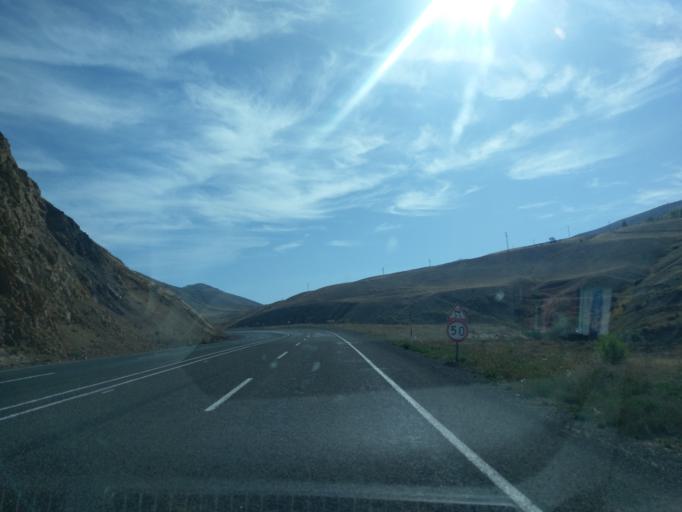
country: TR
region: Sivas
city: Akincilar
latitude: 39.8616
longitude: 38.3406
